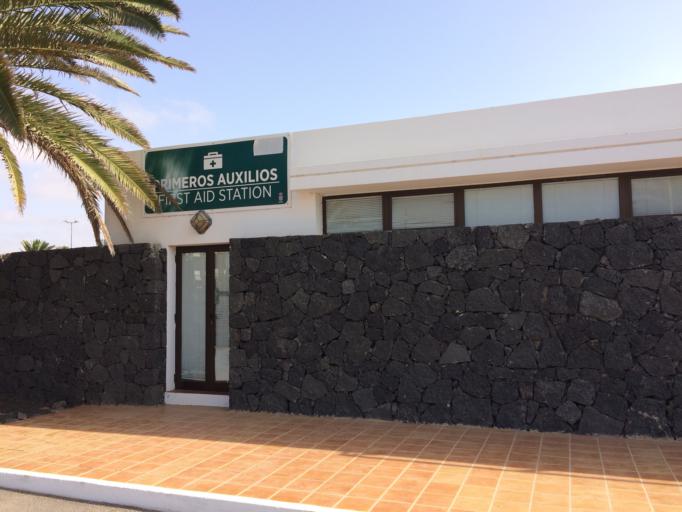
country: ES
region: Canary Islands
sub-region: Provincia de Las Palmas
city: Arrecife
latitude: 29.0001
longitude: -13.4877
